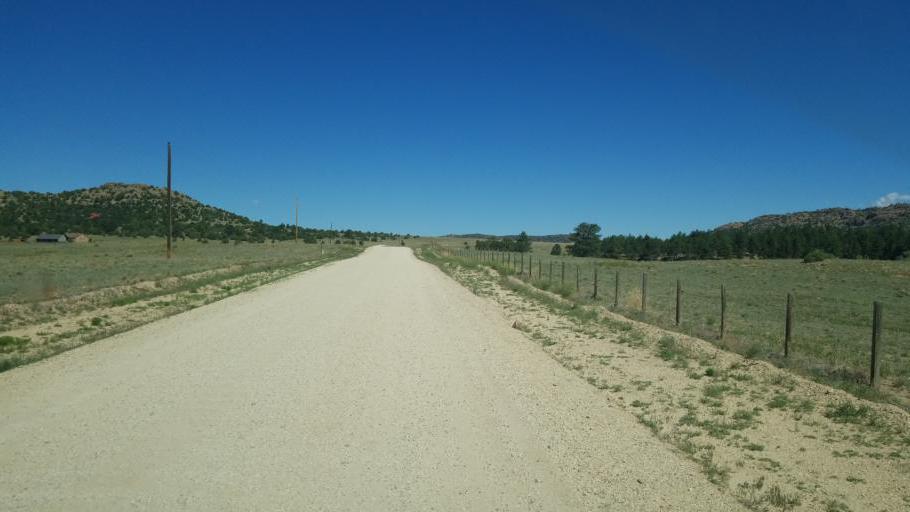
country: US
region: Colorado
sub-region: Custer County
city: Westcliffe
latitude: 38.2175
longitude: -105.4509
